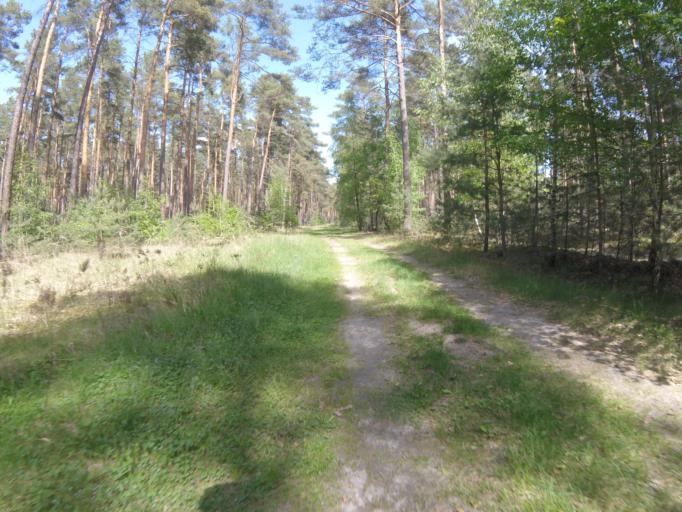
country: DE
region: Brandenburg
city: Schwerin
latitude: 52.1605
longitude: 13.6118
